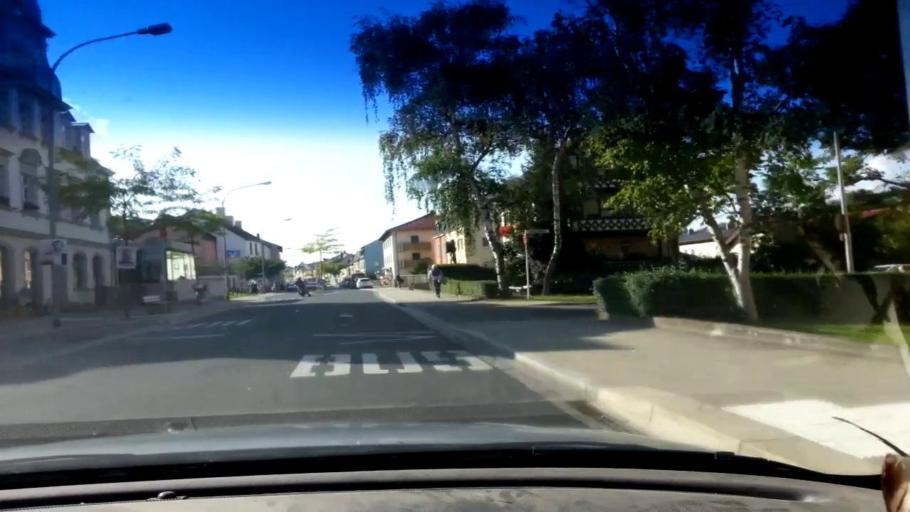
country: DE
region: Bavaria
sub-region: Upper Franconia
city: Bischberg
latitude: 49.9034
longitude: 10.8502
